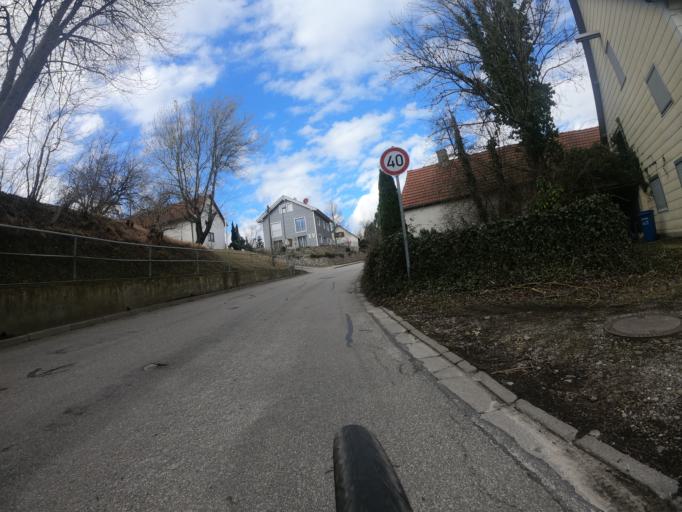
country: DE
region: Bavaria
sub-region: Upper Bavaria
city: Landsberied
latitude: 48.1804
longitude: 11.1837
